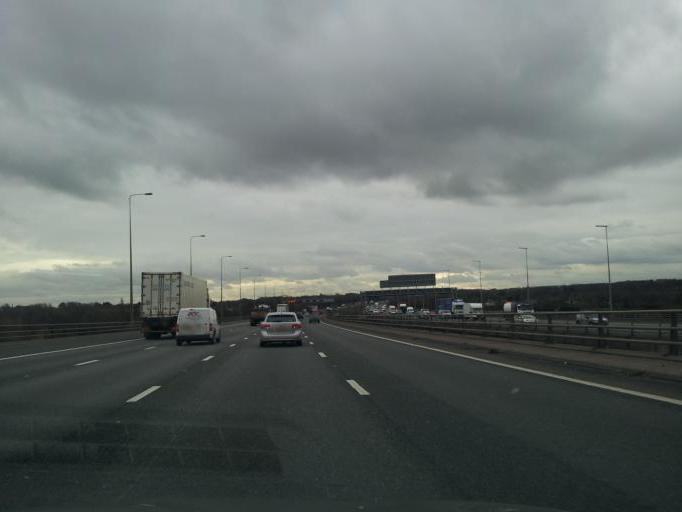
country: GB
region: England
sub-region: Warrington
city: Lymm
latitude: 53.3873
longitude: -2.5048
